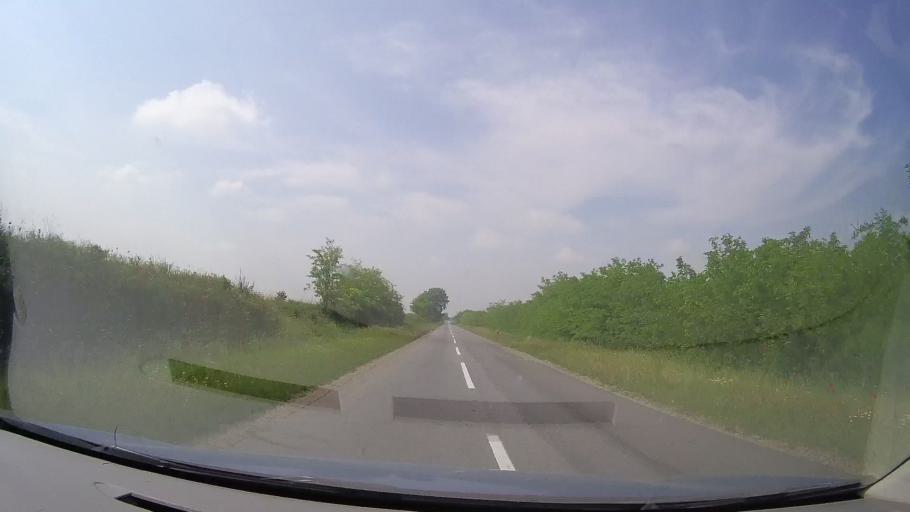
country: RS
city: Padina
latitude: 45.1449
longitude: 20.7417
